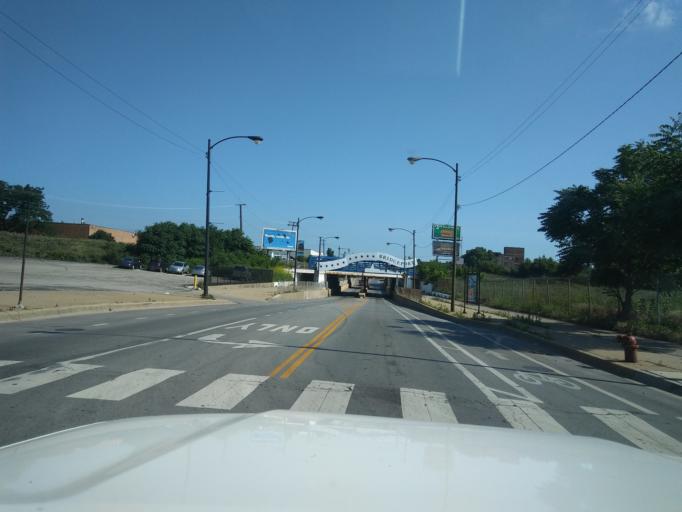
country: US
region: Illinois
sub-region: Cook County
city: Chicago
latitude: 41.8203
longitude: -87.6458
